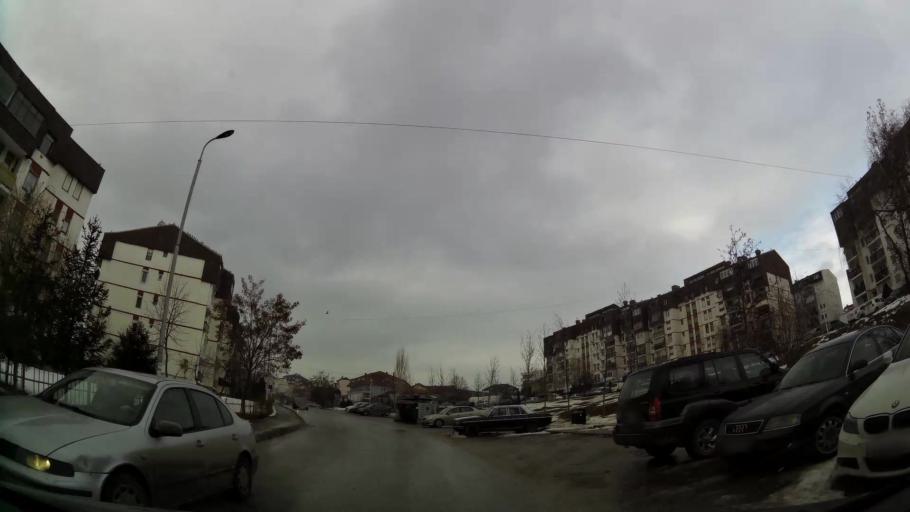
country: XK
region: Pristina
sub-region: Komuna e Prishtines
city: Pristina
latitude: 42.6569
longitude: 21.1816
